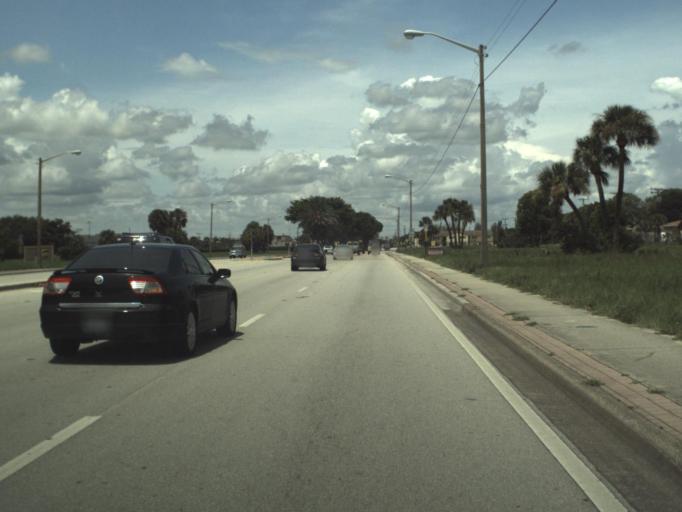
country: US
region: Florida
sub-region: Palm Beach County
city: Riviera Beach
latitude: 26.7810
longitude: -80.0746
